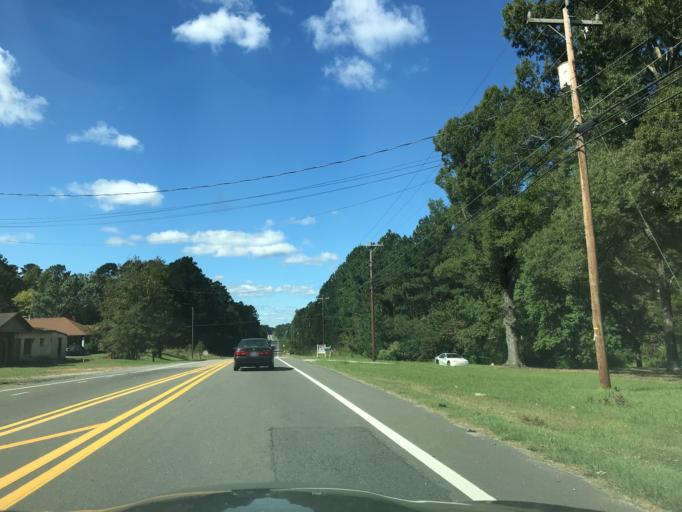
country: US
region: North Carolina
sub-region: Durham County
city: Gorman
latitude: 35.9770
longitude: -78.7952
